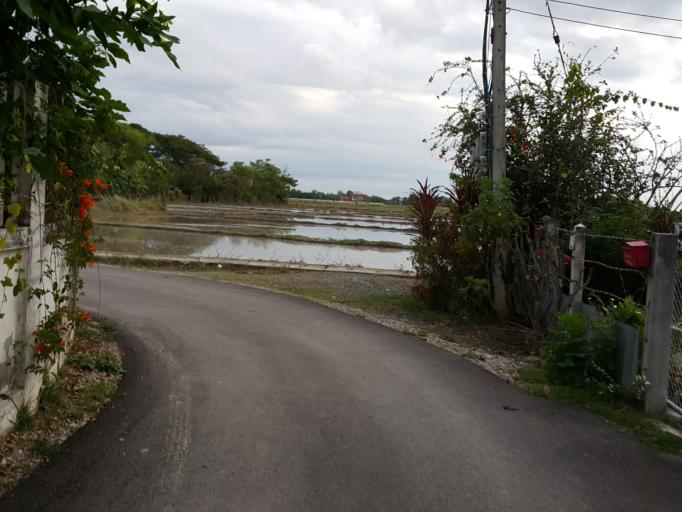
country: TH
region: Chiang Mai
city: San Sai
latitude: 18.8495
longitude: 99.1165
